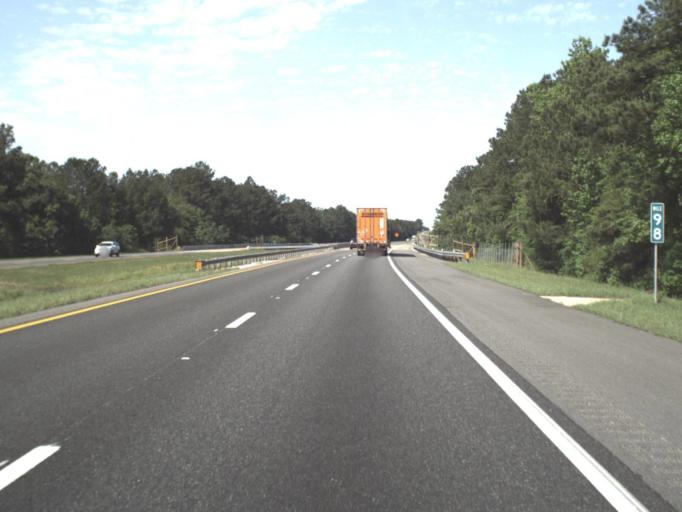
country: US
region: Florida
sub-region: Walton County
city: DeFuniak Springs
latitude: 30.7288
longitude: -85.9008
